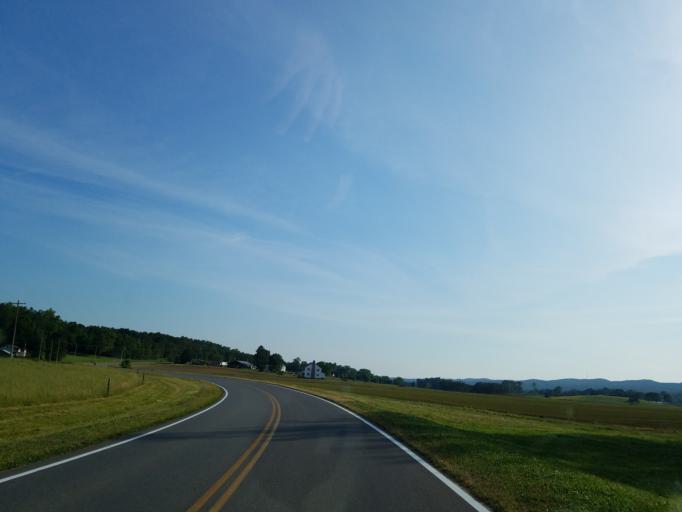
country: US
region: Georgia
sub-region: Chattooga County
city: Trion
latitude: 34.5165
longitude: -85.2305
